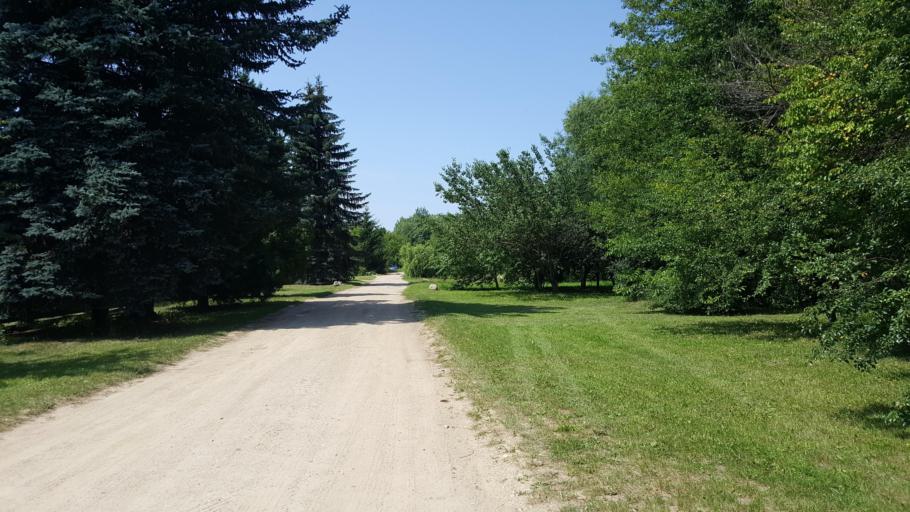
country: BY
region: Brest
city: Zhabinka
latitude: 52.1912
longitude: 23.9999
